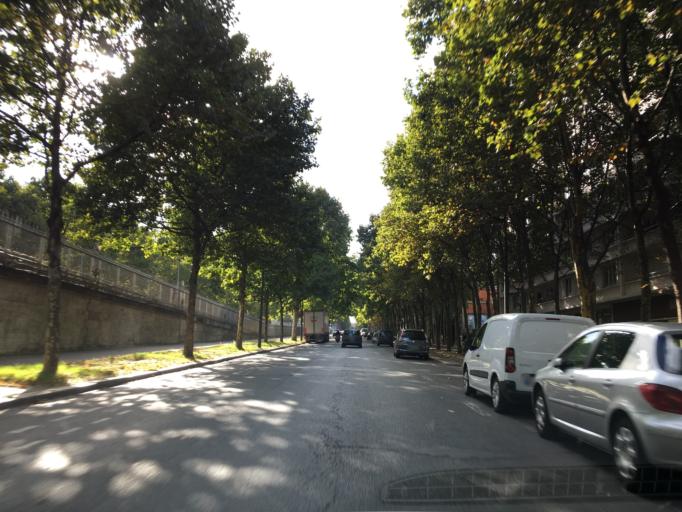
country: FR
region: Ile-de-France
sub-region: Departement du Val-de-Marne
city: Gentilly
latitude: 48.8322
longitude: 2.3400
